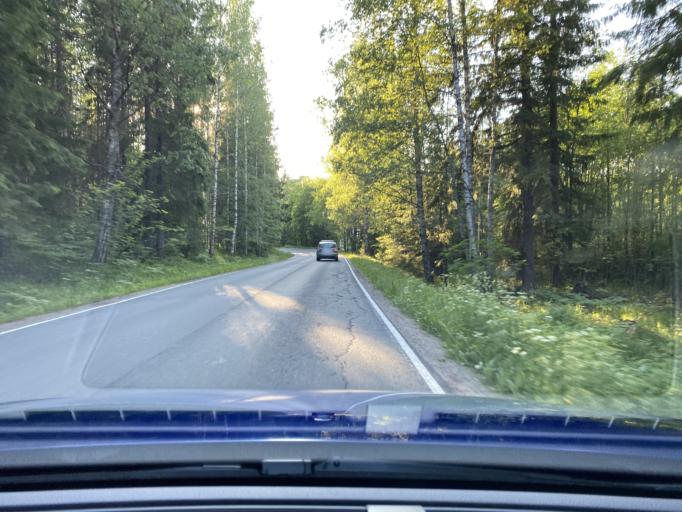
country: FI
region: Haeme
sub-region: Riihimaeki
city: Riihimaeki
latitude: 60.7293
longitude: 24.6915
